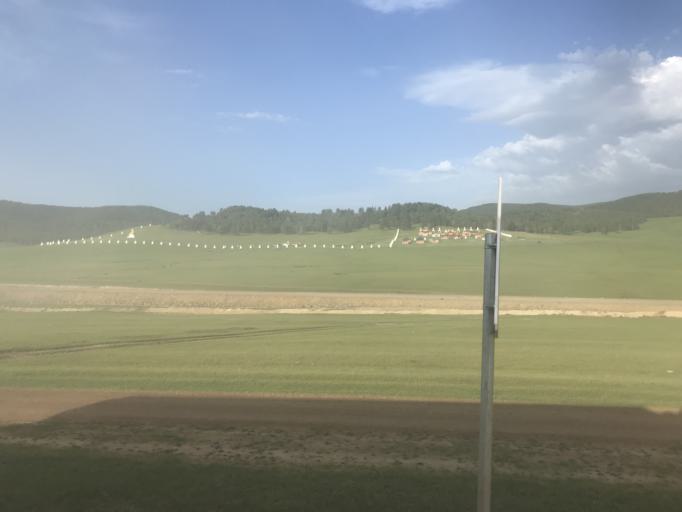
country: MN
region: Central Aimak
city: Bornuur
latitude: 48.5209
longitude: 106.1322
